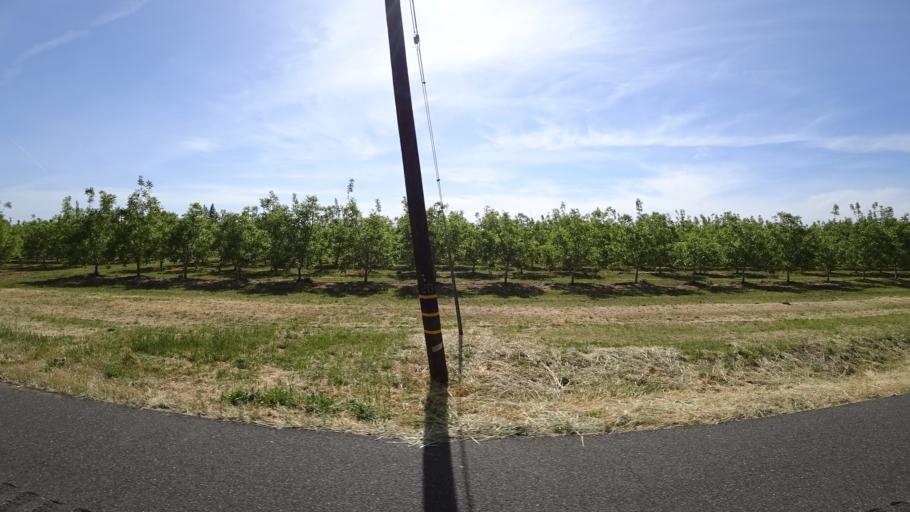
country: US
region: California
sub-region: Tehama County
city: Gerber
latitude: 40.0994
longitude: -122.1031
